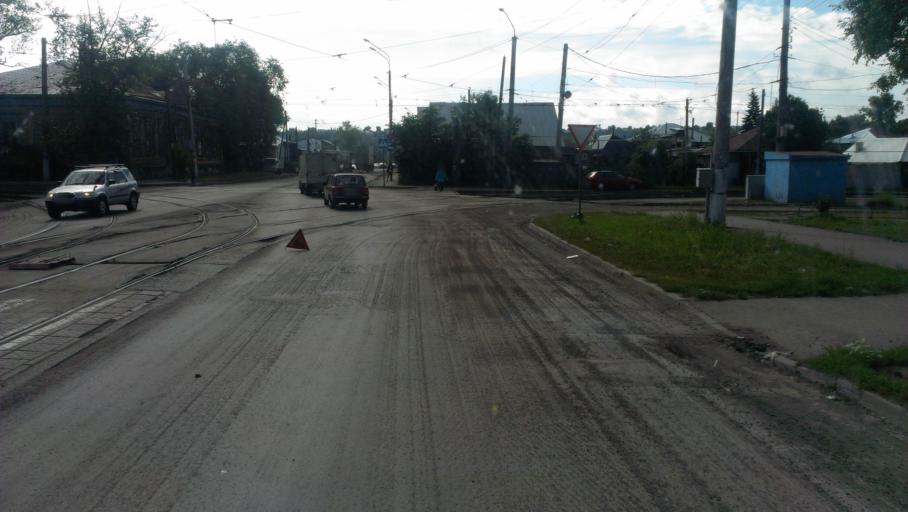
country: RU
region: Altai Krai
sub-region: Gorod Barnaulskiy
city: Barnaul
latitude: 53.3274
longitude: 83.7630
